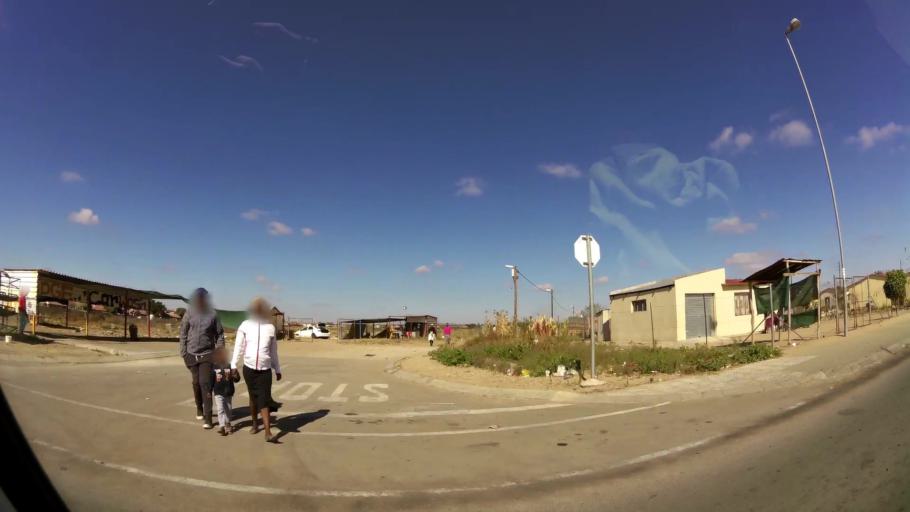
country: ZA
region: Limpopo
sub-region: Capricorn District Municipality
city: Polokwane
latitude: -23.8602
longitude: 29.3984
